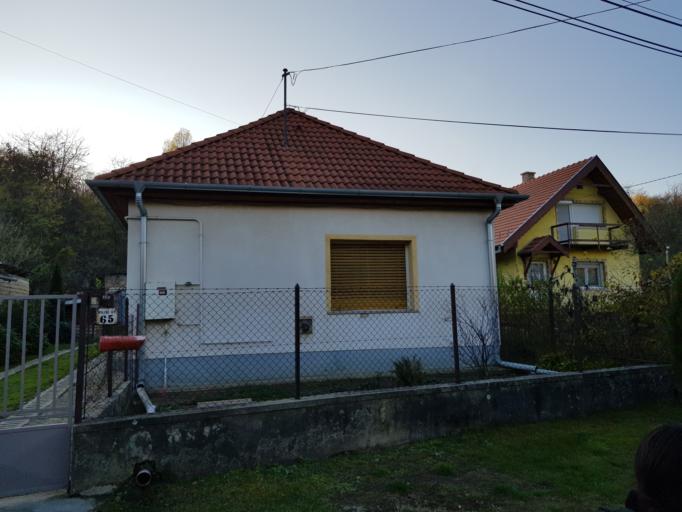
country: HU
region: Pest
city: Gomba
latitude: 47.3462
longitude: 19.5395
